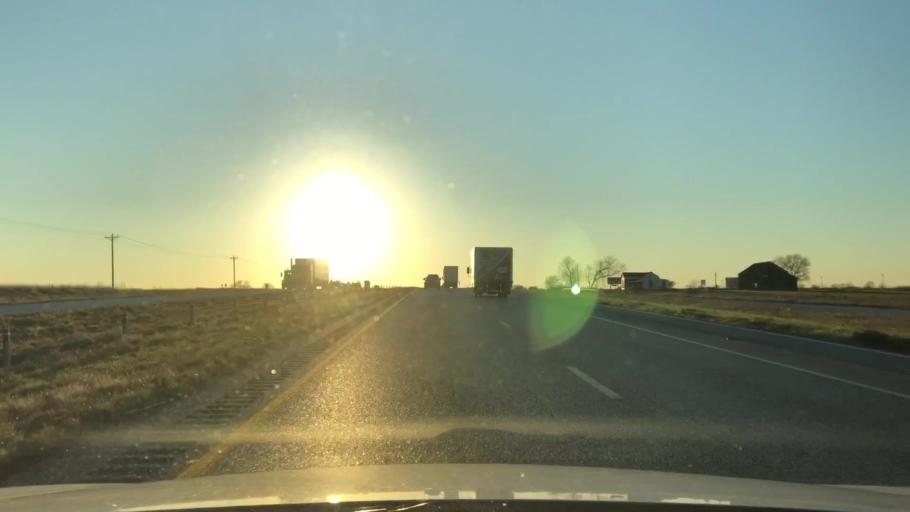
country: US
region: Texas
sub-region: Guadalupe County
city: Marion
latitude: 29.5246
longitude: -98.1251
